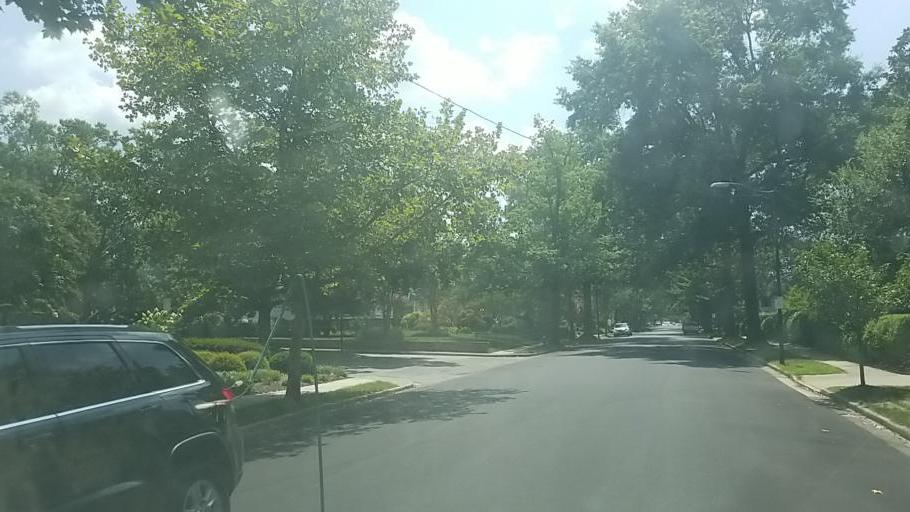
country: US
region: Maryland
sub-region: Talbot County
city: Easton
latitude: 38.7694
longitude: -76.0743
